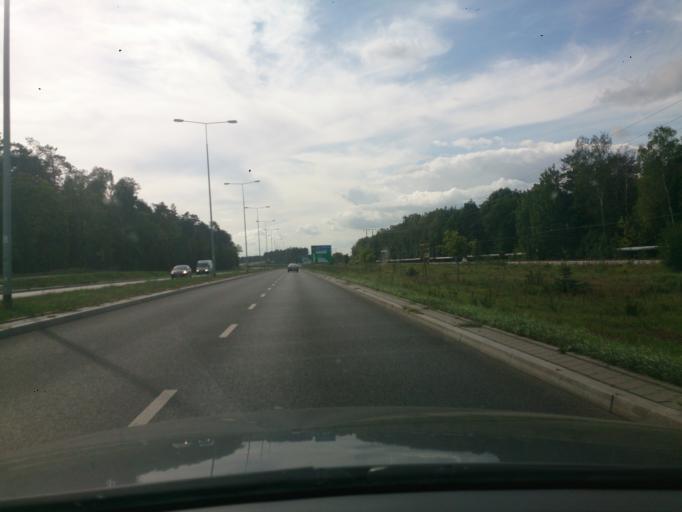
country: PL
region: Kujawsko-Pomorskie
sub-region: Grudziadz
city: Grudziadz
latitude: 53.4562
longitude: 18.7393
